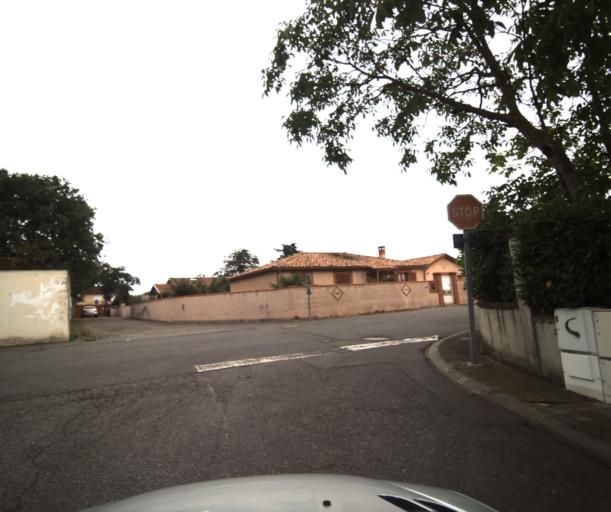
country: FR
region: Midi-Pyrenees
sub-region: Departement de la Haute-Garonne
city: Pinsaguel
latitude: 43.4981
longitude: 1.3937
